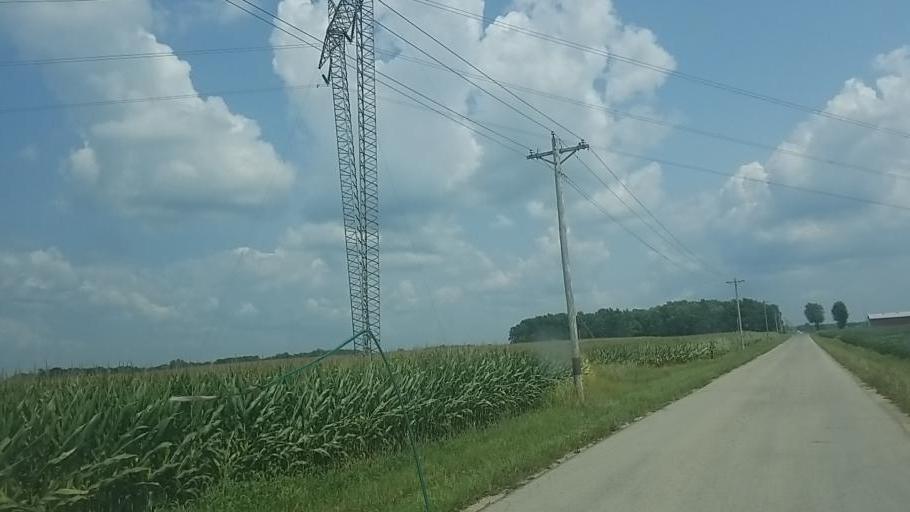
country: US
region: Ohio
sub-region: Wyandot County
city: Upper Sandusky
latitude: 40.9209
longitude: -83.1738
